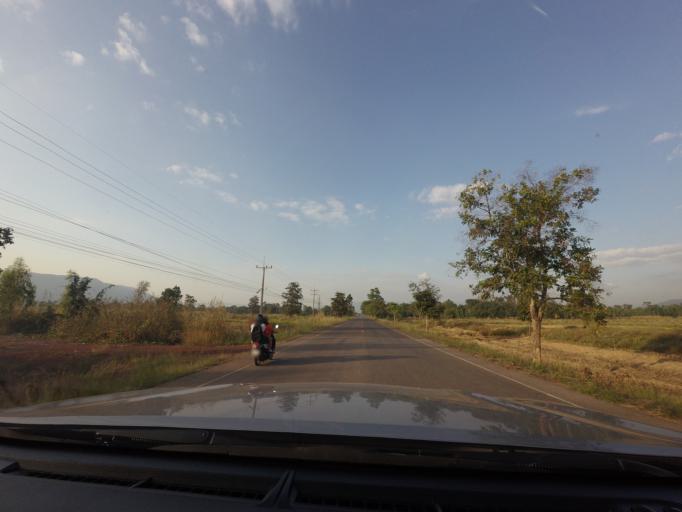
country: TH
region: Phitsanulok
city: Noen Maprang
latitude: 16.6234
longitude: 100.6187
